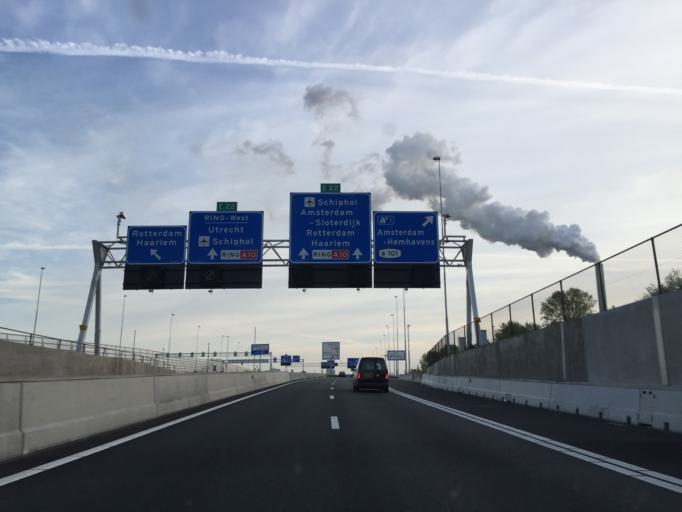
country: NL
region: North Holland
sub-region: Gemeente Zaanstad
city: Zaandam
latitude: 52.4092
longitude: 4.8590
